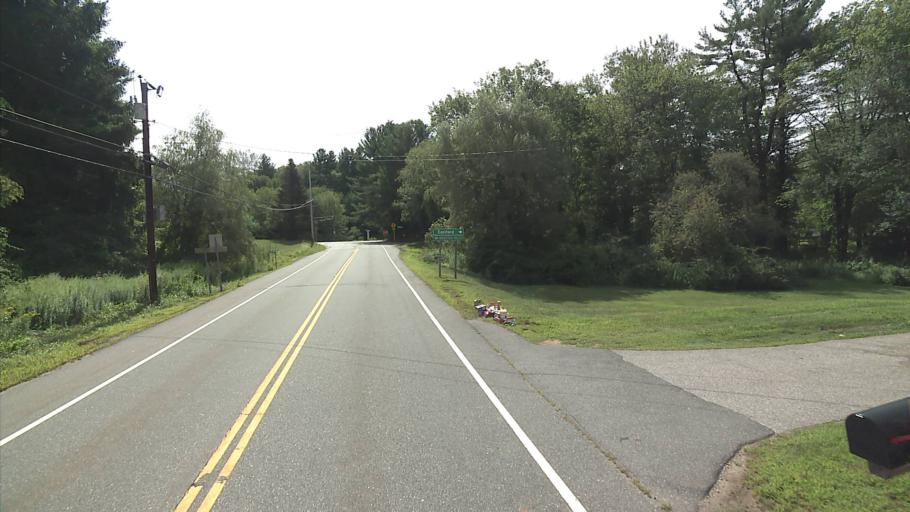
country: US
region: Connecticut
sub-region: Windham County
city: South Woodstock
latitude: 41.9300
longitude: -72.0842
